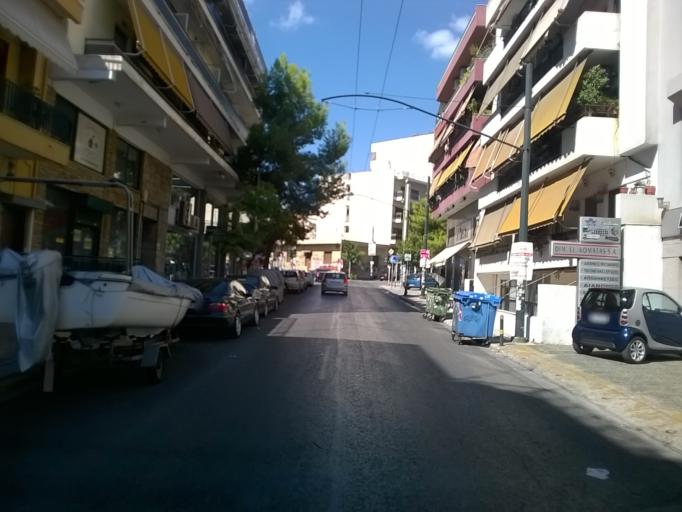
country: GR
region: Attica
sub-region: Nomos Piraios
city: Nikaia
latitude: 37.9699
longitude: 23.6497
